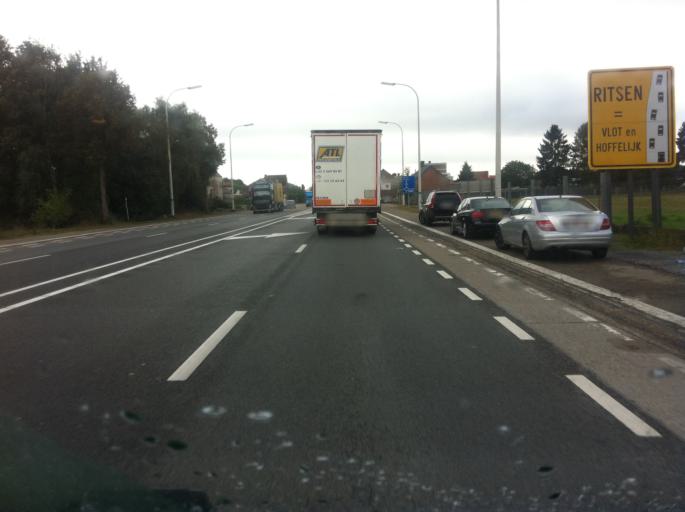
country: BE
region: Flanders
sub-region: Provincie Limburg
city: Maasmechelen
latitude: 50.9301
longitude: 5.6886
